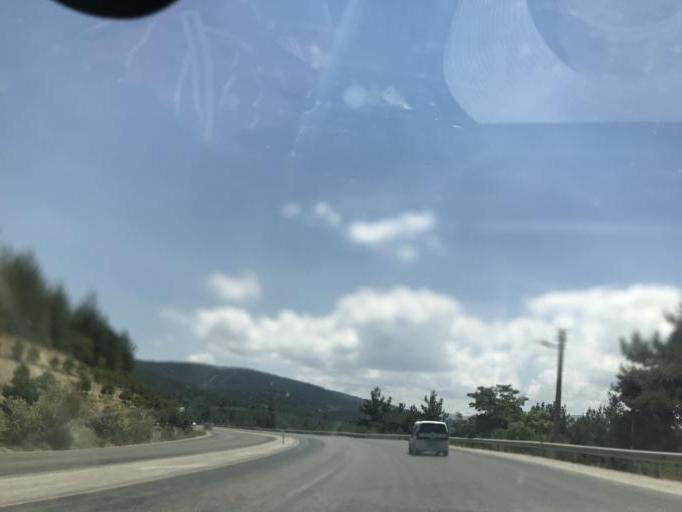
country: TR
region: Denizli
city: Honaz
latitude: 37.6780
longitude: 29.2238
